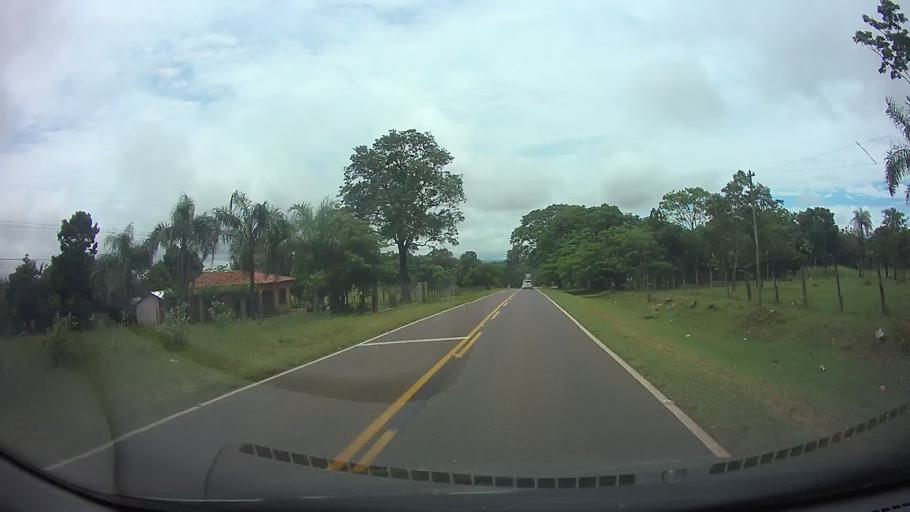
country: PY
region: Paraguari
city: Acahay
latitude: -25.9528
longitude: -57.0925
